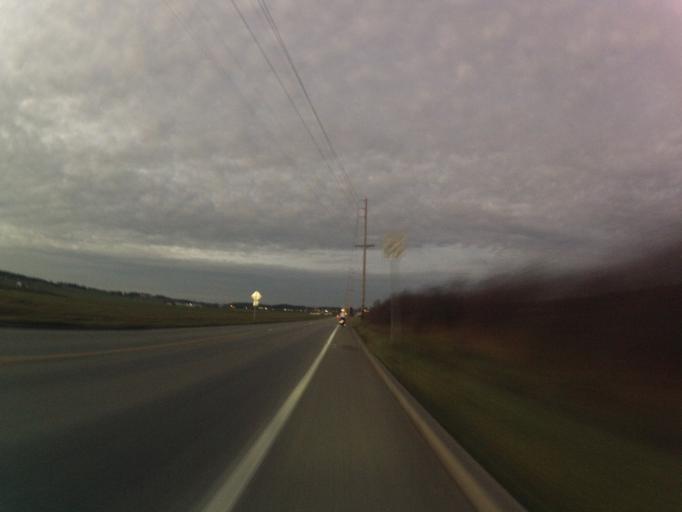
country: US
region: Washington
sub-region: Island County
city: Coupeville
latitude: 48.1917
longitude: -122.6861
